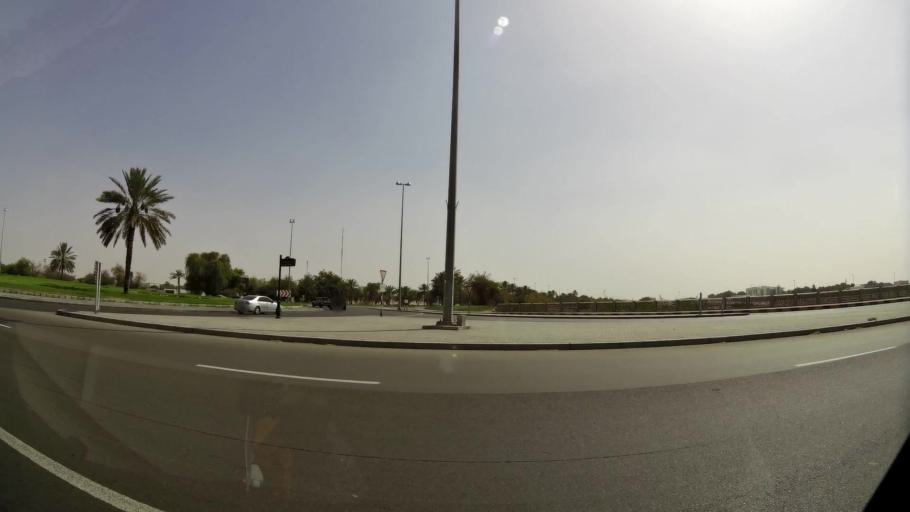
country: AE
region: Abu Dhabi
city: Al Ain
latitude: 24.2178
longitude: 55.6831
